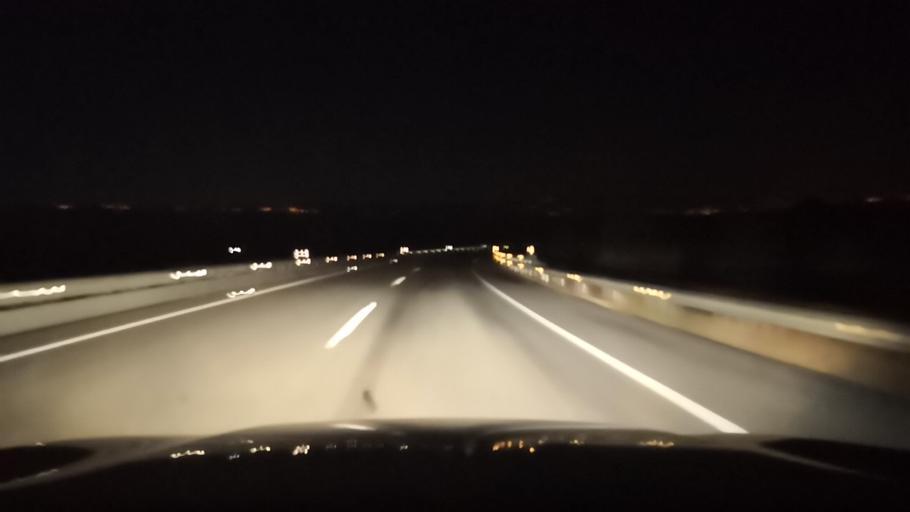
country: ES
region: Galicia
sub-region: Provincia de Ourense
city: Oimbra
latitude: 41.8482
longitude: -7.4125
